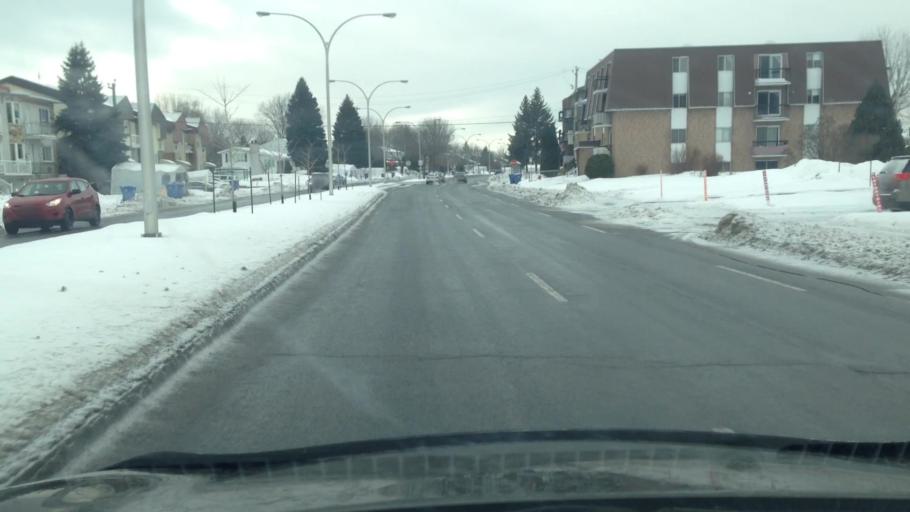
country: CA
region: Quebec
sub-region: Monteregie
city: Brossard
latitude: 45.4701
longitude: -73.4453
